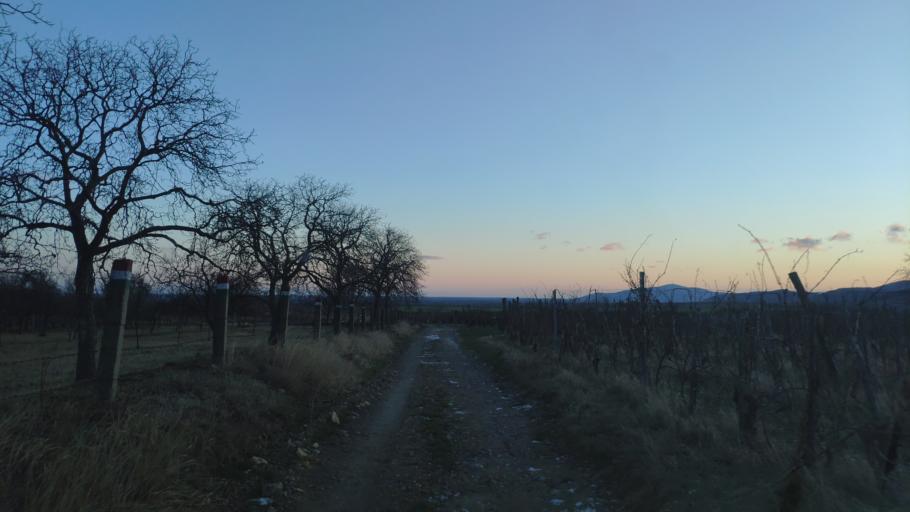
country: HU
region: Borsod-Abauj-Zemplen
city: Olaszliszka
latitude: 48.2709
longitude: 21.3986
